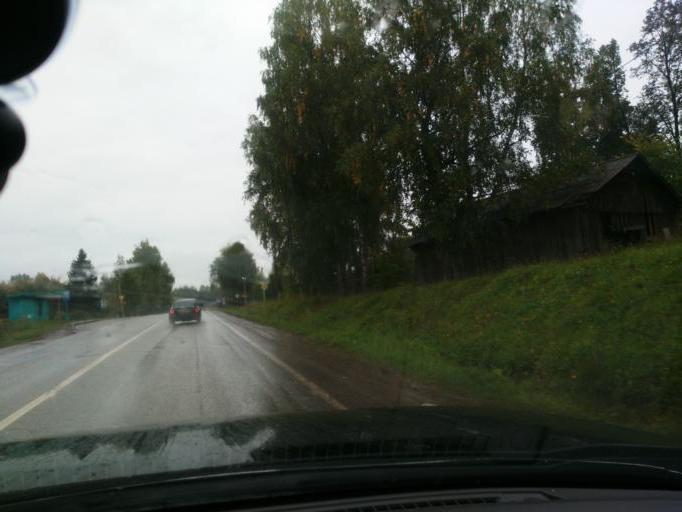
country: RU
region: Perm
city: Osa
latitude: 57.3689
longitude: 55.6070
